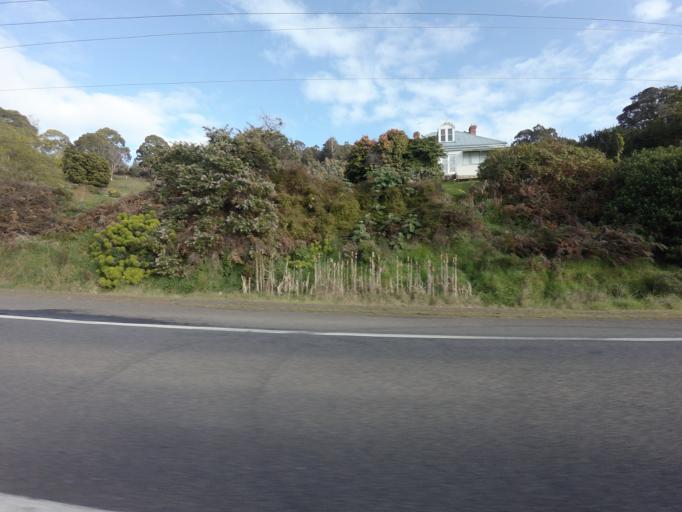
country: AU
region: Tasmania
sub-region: Huon Valley
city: Franklin
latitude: -43.1047
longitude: 147.0005
